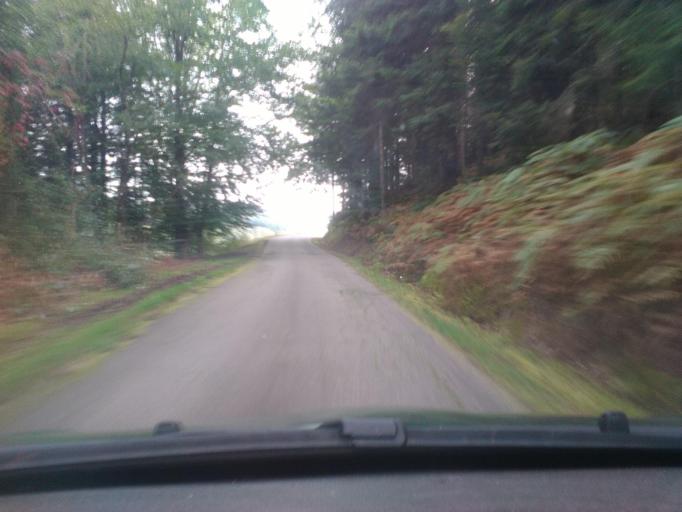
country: FR
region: Lorraine
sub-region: Departement des Vosges
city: Corcieux
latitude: 48.2110
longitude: 6.8794
